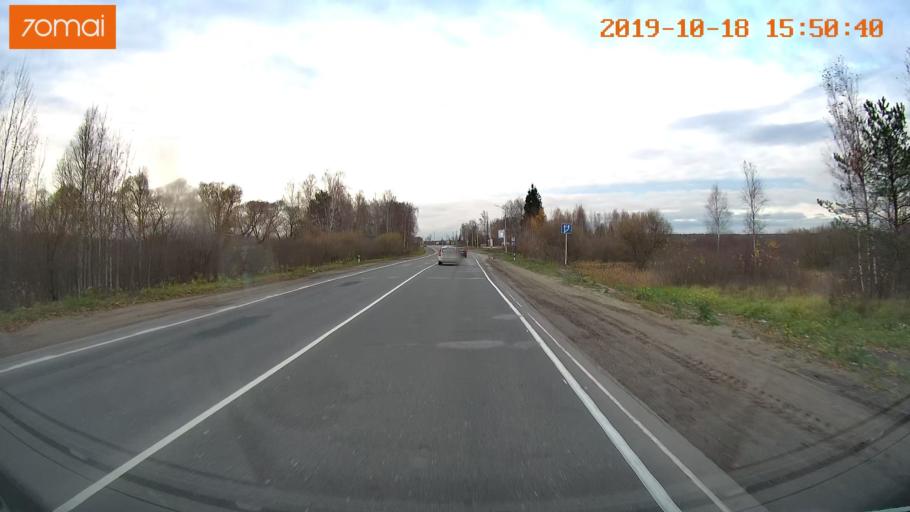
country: RU
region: Vladimir
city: Kommunar
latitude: 56.0347
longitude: 40.5572
